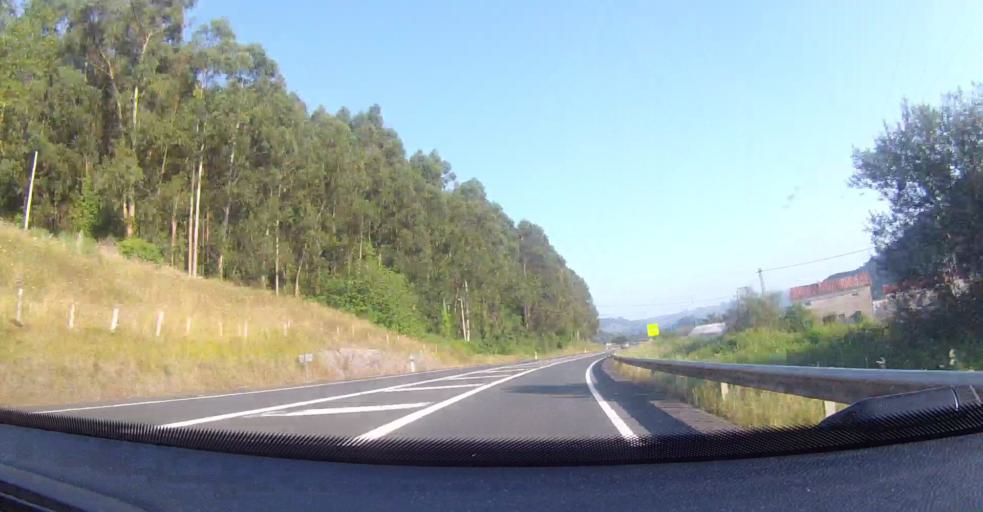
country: ES
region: Cantabria
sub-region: Provincia de Cantabria
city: Colindres
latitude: 43.3835
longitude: -3.4395
